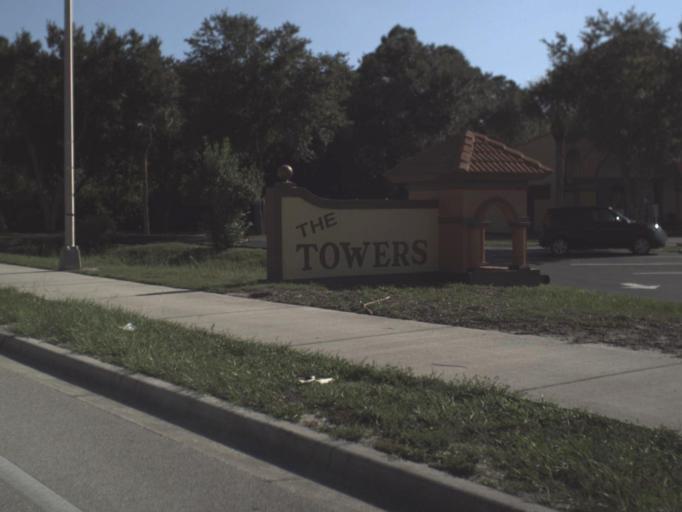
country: US
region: Florida
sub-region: Sarasota County
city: Englewood
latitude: 26.9737
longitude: -82.3540
